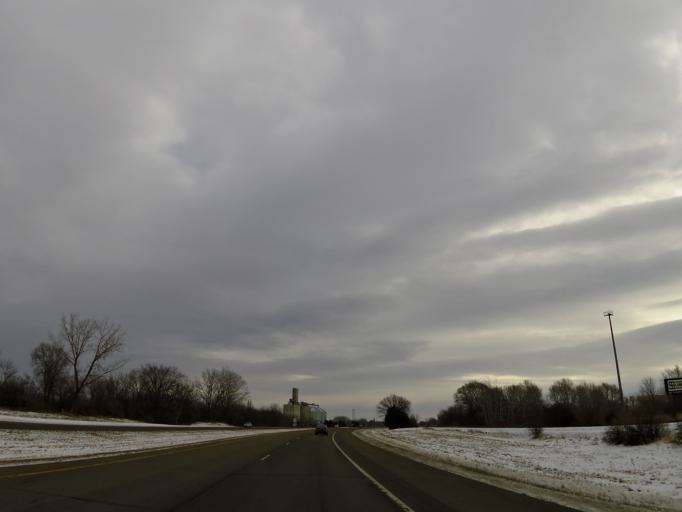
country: US
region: Minnesota
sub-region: Scott County
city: Shakopee
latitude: 44.8027
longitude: -93.4859
